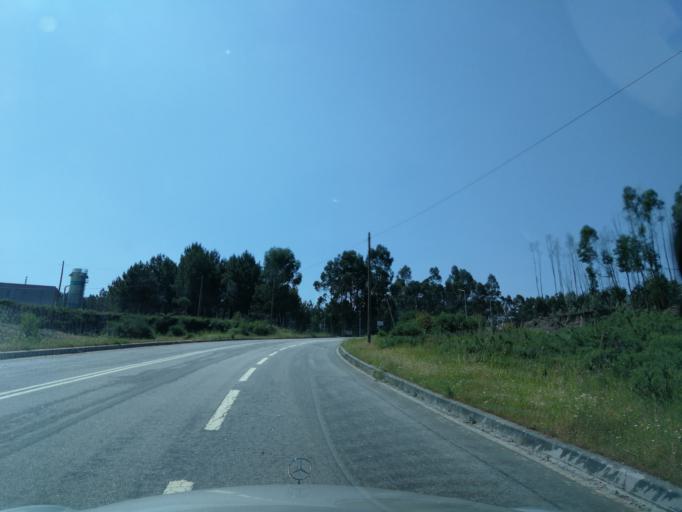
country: PT
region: Braga
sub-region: Braga
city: Adaufe
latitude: 41.5587
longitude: -8.3546
